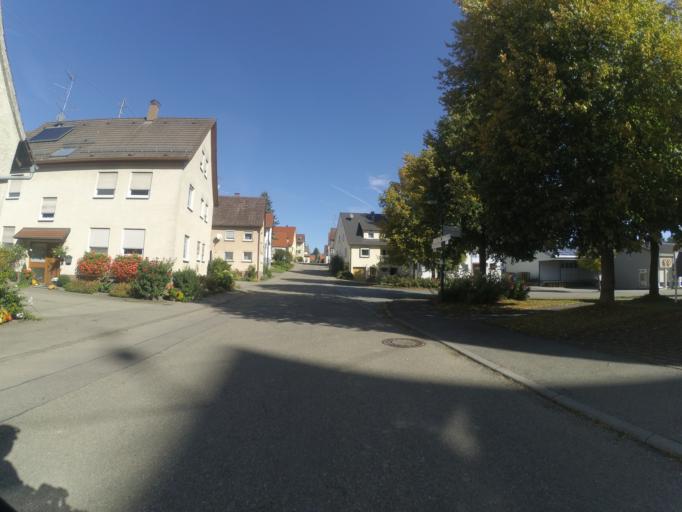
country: DE
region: Baden-Wuerttemberg
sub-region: Tuebingen Region
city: Ballendorf
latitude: 48.5543
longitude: 10.0771
